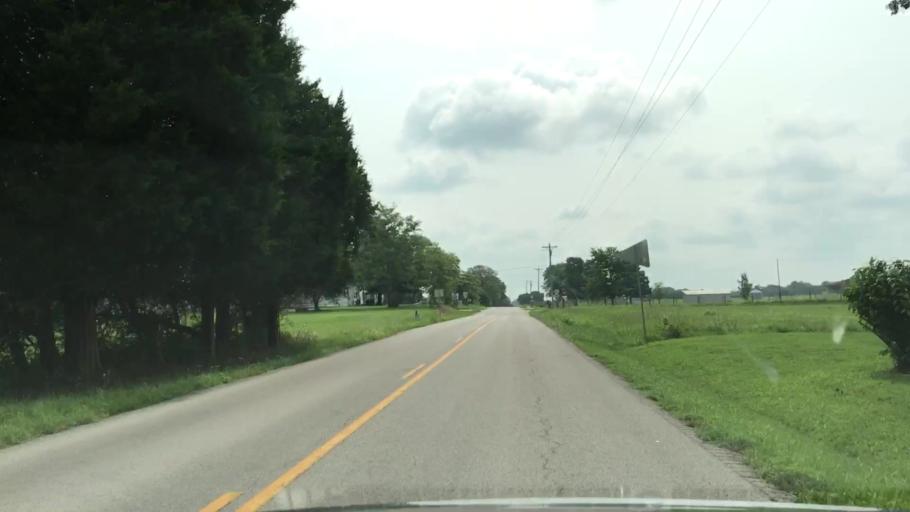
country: US
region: Kentucky
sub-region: Edmonson County
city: Brownsville
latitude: 37.1333
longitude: -86.1713
